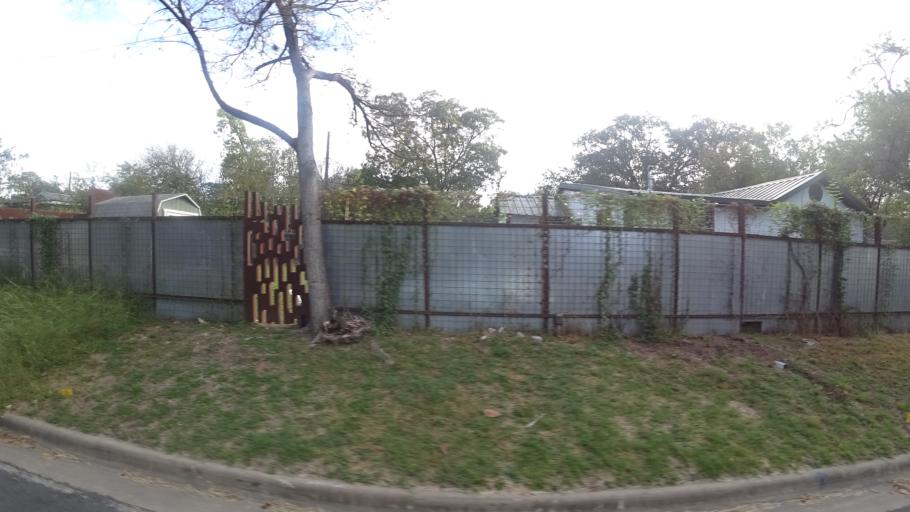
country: US
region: Texas
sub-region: Travis County
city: Austin
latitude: 30.2803
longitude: -97.7051
